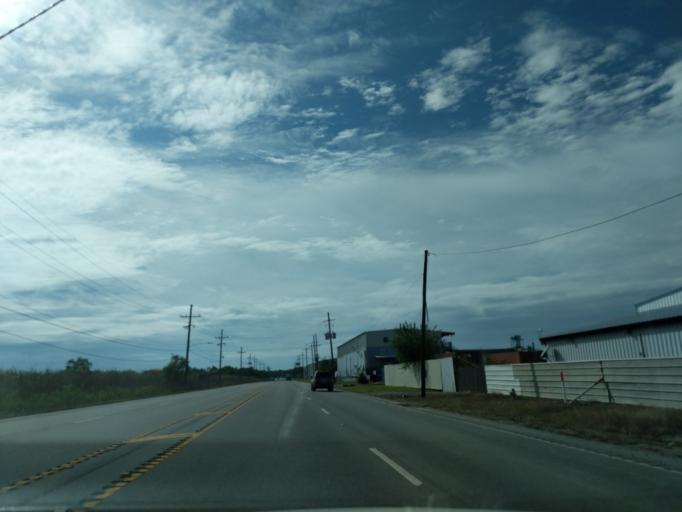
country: US
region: Louisiana
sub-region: Saint Tammany Parish
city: Eden Isle
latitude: 30.0768
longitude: -89.8483
